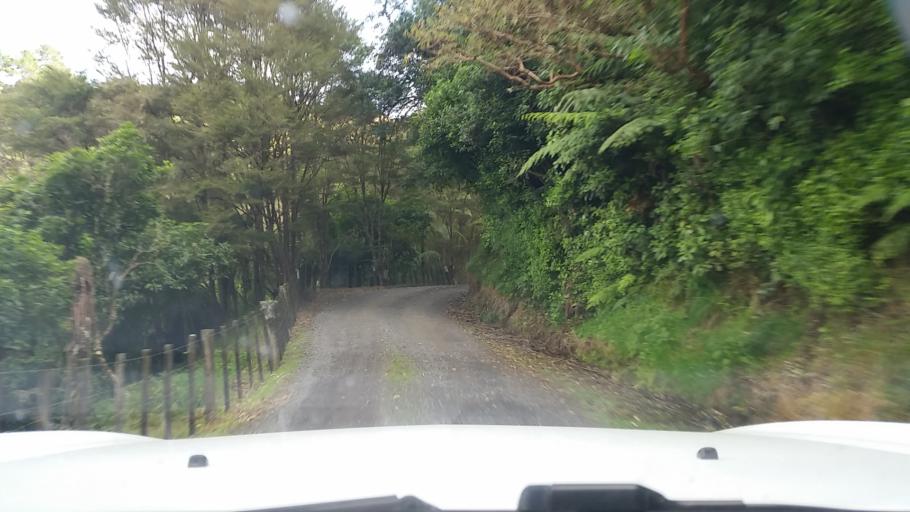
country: NZ
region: Waikato
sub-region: Hauraki District
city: Ngatea
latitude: -37.4702
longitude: 175.4564
